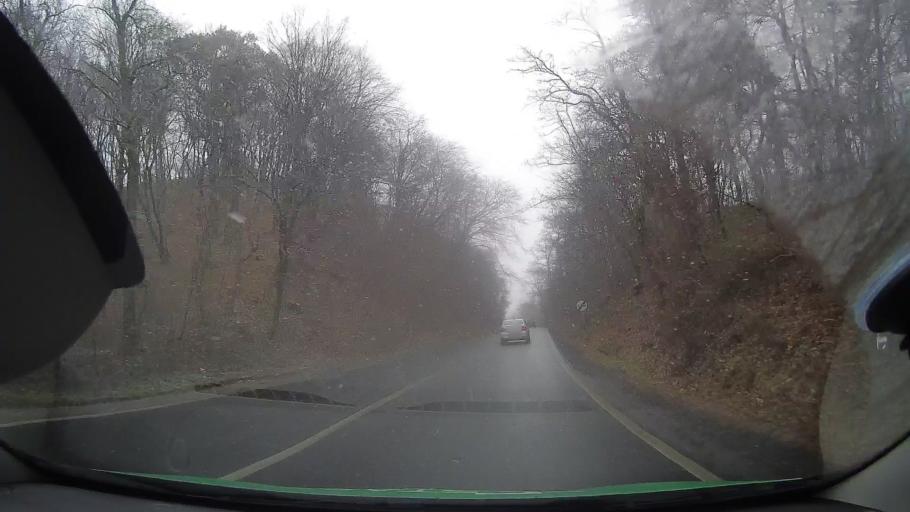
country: RO
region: Sibiu
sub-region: Municipiul Medias
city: Medias
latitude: 46.1847
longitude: 24.3354
